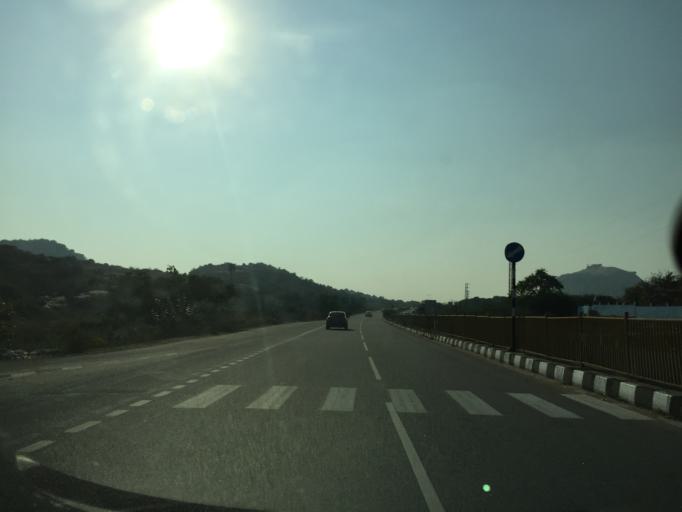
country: IN
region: Telangana
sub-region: Nalgonda
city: Bhongir
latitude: 17.5148
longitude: 78.9134
